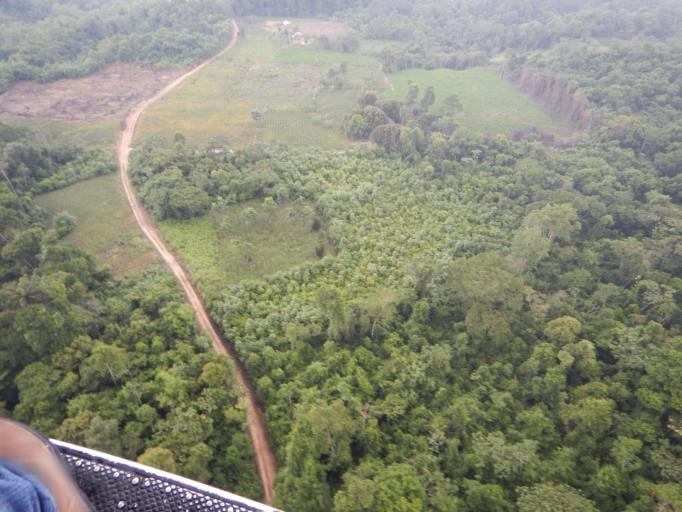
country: BO
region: Cochabamba
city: Chimore
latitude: -17.0452
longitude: -64.8162
